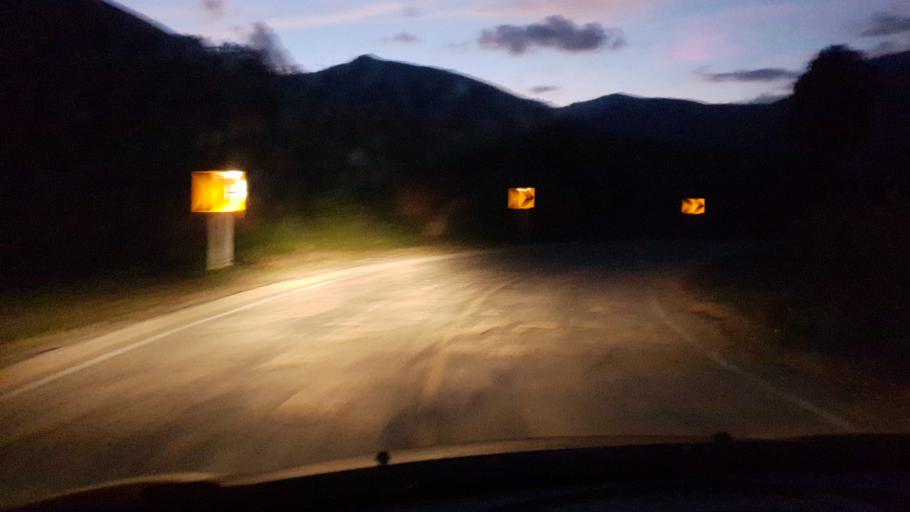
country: TH
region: Mae Hong Son
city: Khun Yuam
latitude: 18.7469
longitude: 98.1990
